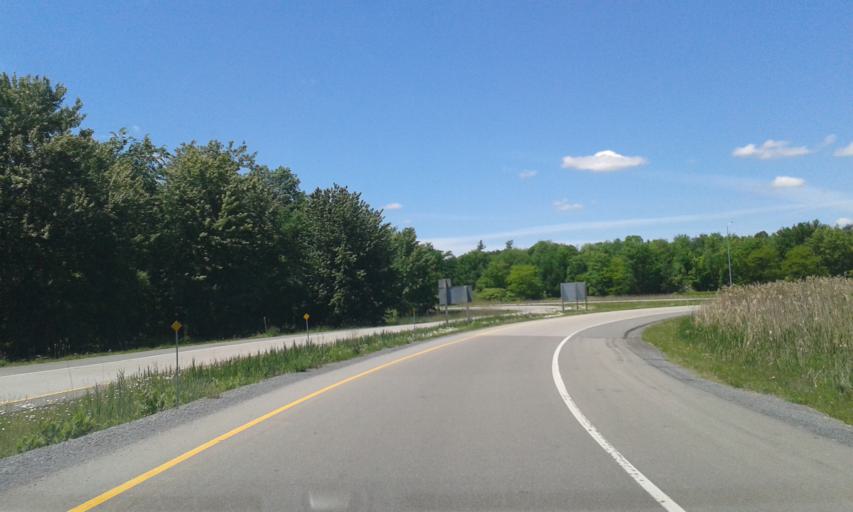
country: US
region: New York
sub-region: St. Lawrence County
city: Massena
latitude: 45.0448
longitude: -74.9064
